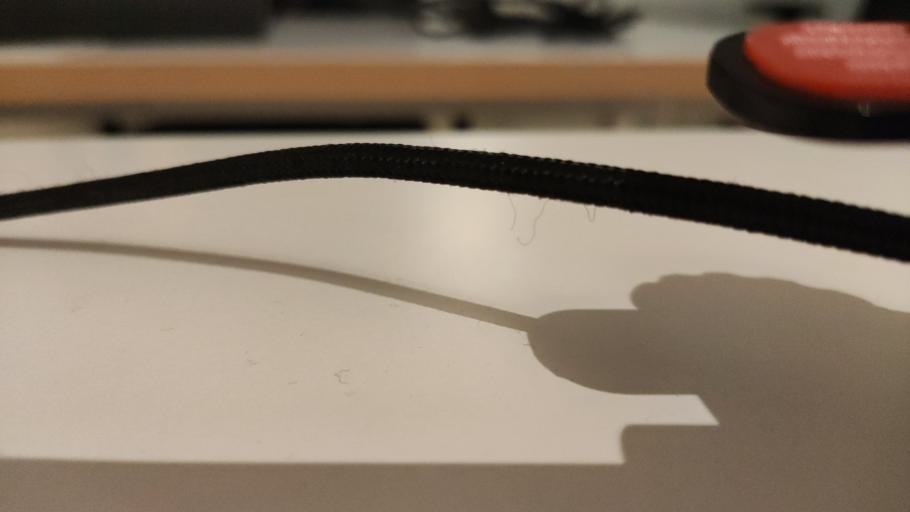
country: RU
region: Moskovskaya
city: Kurovskoye
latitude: 55.5406
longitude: 38.8730
